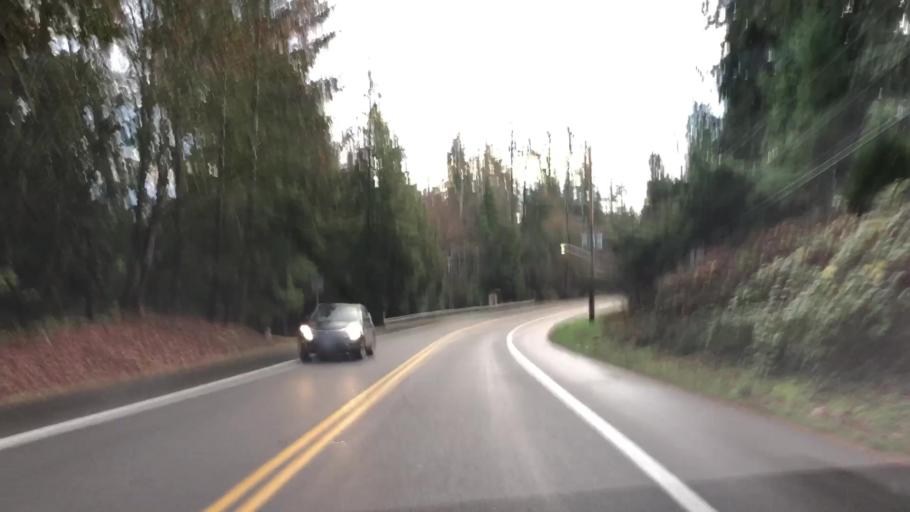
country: US
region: Washington
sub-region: King County
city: City of Sammamish
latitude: 47.6352
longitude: -122.0392
